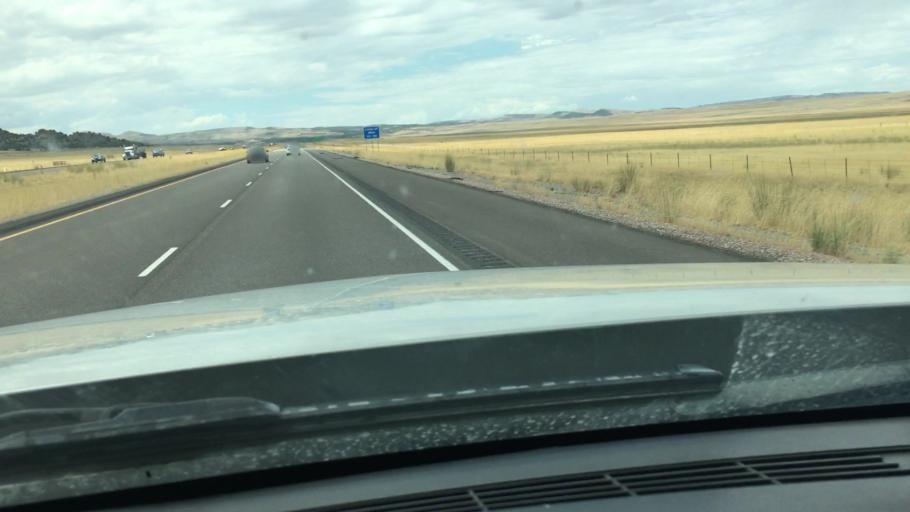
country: US
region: Utah
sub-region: Millard County
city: Fillmore
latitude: 38.7785
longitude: -112.5404
